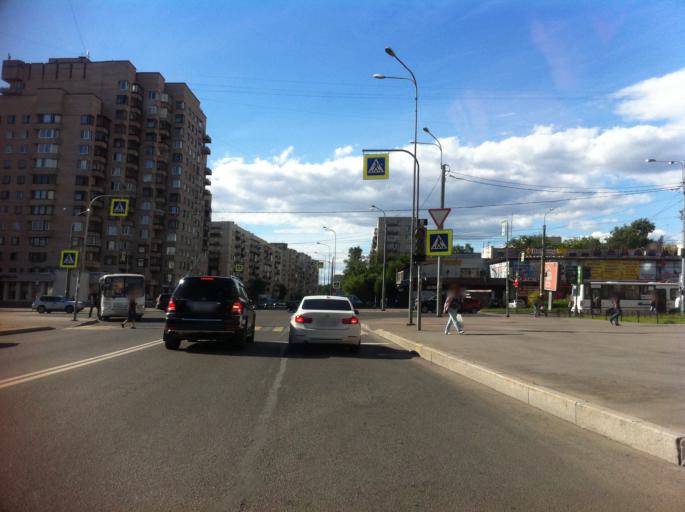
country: RU
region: St.-Petersburg
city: Dachnoye
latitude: 59.8397
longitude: 30.2391
